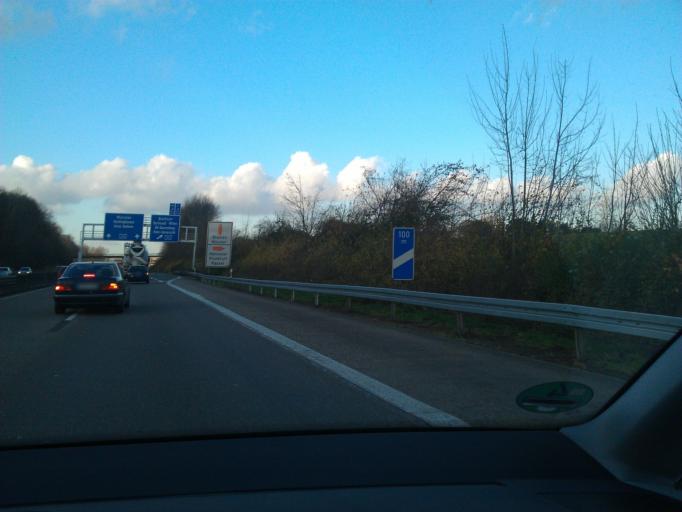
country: DE
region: North Rhine-Westphalia
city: Witten
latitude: 51.4490
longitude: 7.2928
